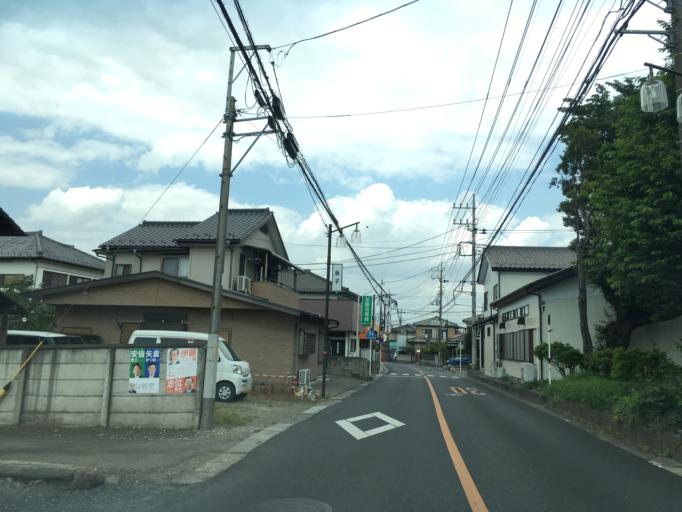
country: JP
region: Saitama
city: Sayama
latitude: 35.8644
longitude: 139.4183
